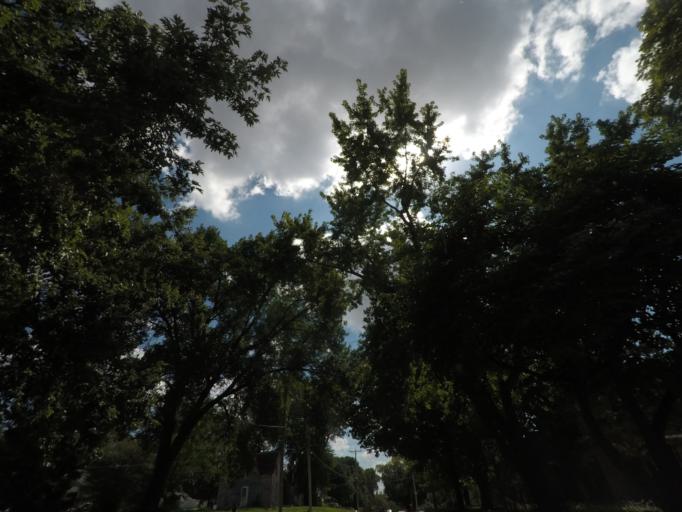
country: US
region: Iowa
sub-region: Story County
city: Nevada
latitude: 42.0220
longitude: -93.4591
